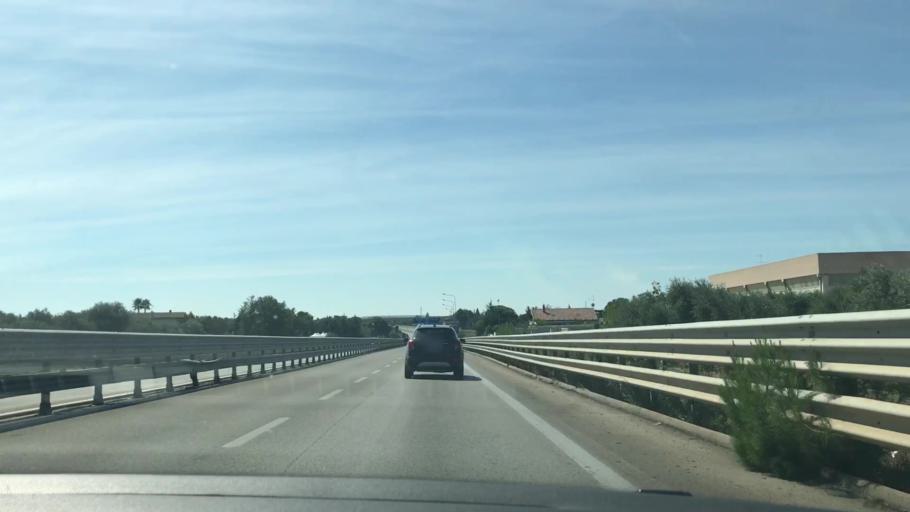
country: IT
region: Apulia
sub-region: Provincia di Bari
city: Altamura
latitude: 40.8014
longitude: 16.5547
